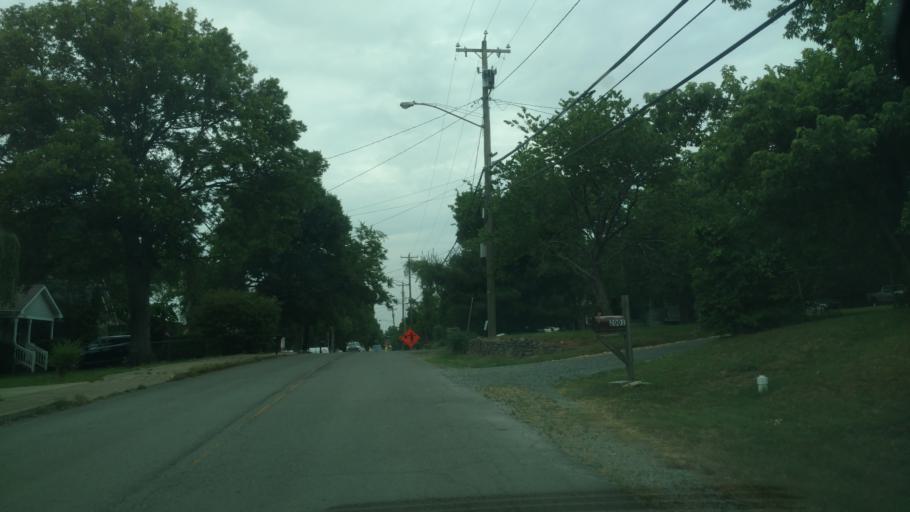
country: US
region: Tennessee
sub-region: Davidson County
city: Nashville
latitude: 36.1937
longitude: -86.7329
